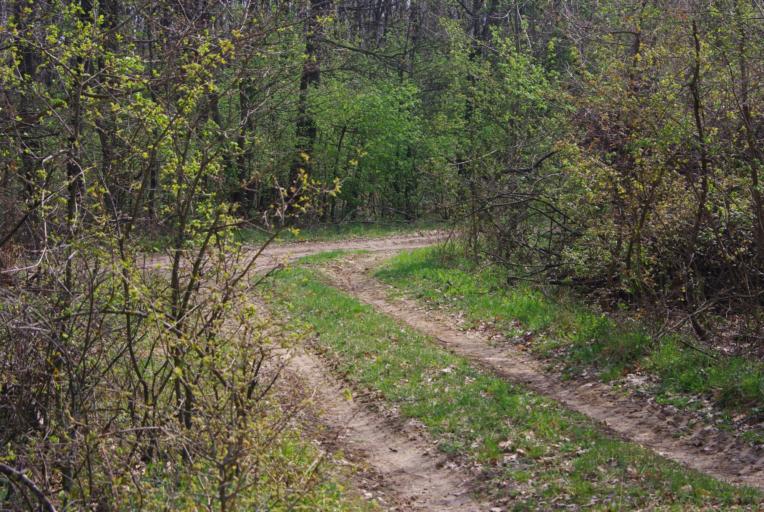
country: HU
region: Fejer
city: Csakvar
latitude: 47.4295
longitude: 18.4566
